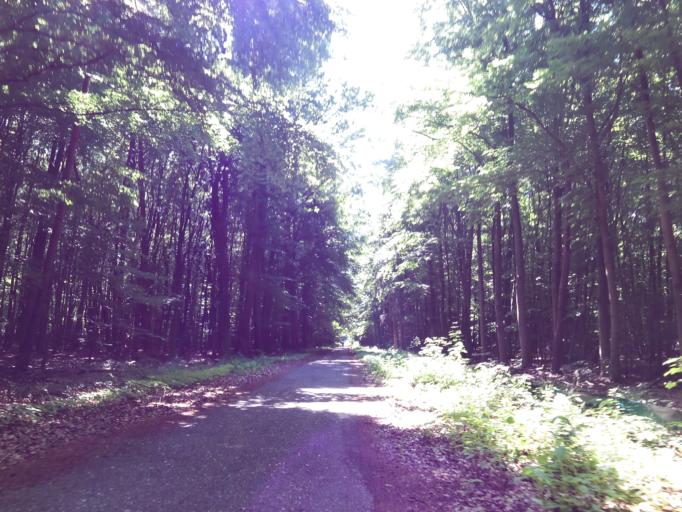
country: DE
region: Hesse
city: Morfelden-Walldorf
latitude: 50.0101
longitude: 8.6271
